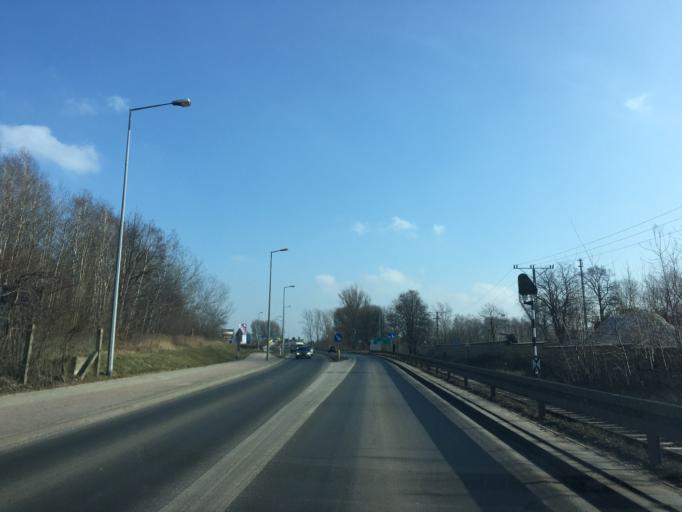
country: PL
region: Lower Silesian Voivodeship
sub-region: Powiat boleslawiecki
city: Boleslawiec
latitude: 51.2690
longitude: 15.5737
